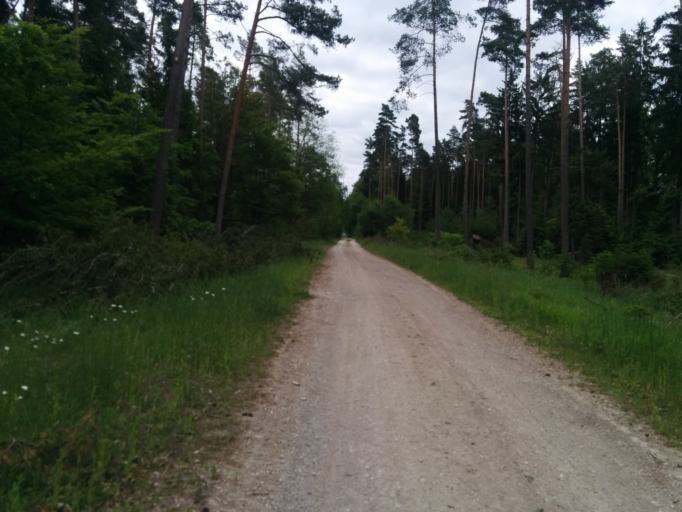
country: DE
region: Bavaria
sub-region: Regierungsbezirk Mittelfranken
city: Buckenhof
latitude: 49.5503
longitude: 11.0562
